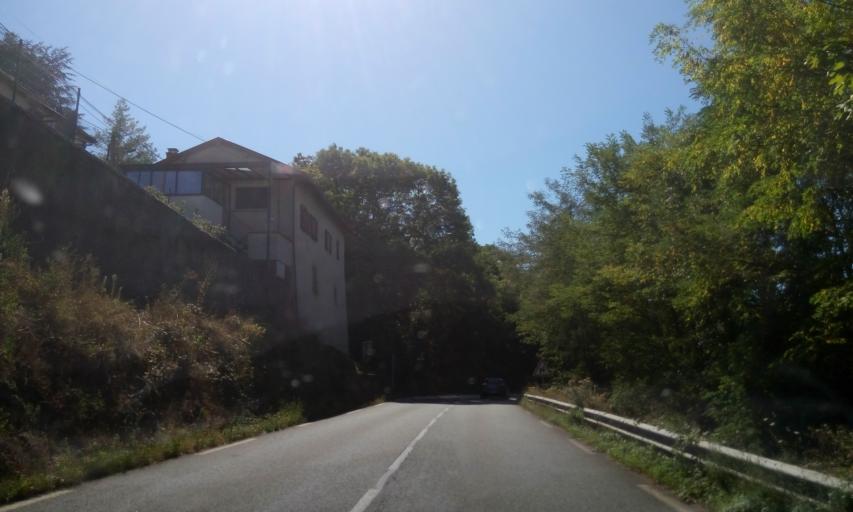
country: FR
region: Rhone-Alpes
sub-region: Departement du Rhone
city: Saint-Verand
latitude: 45.9437
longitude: 4.5395
